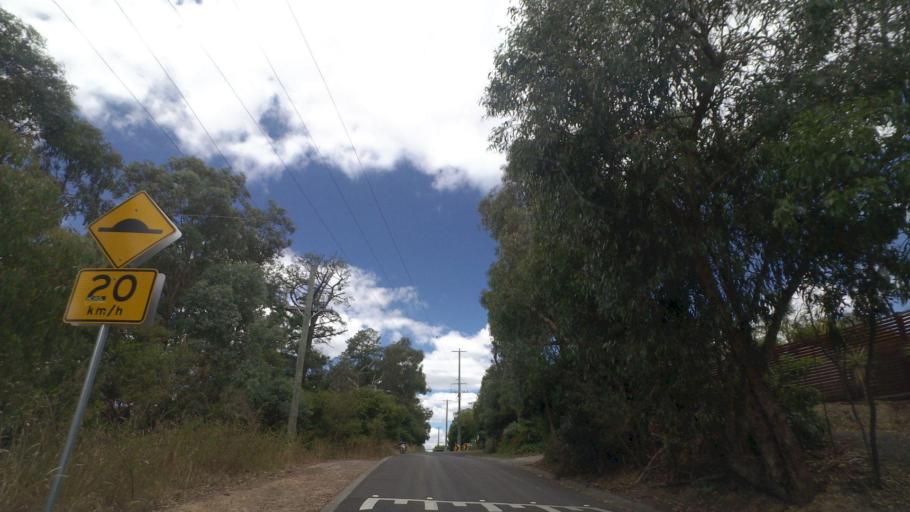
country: AU
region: Victoria
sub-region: Maroondah
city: Warranwood
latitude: -37.7663
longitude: 145.2542
